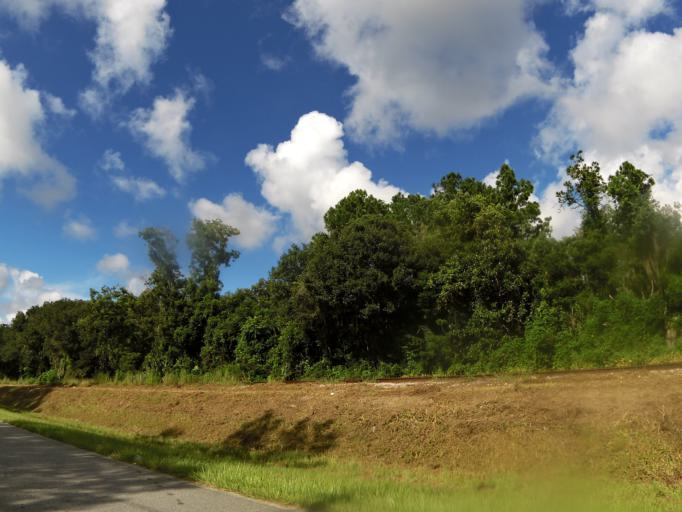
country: US
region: Georgia
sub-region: Camden County
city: Kingsland
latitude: 30.8044
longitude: -81.6924
